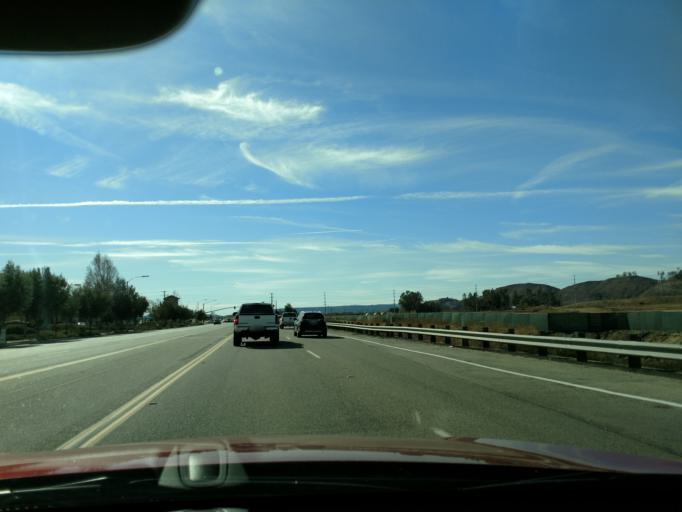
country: US
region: California
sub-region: Riverside County
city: Murrieta Hot Springs
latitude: 33.5939
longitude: -117.1229
